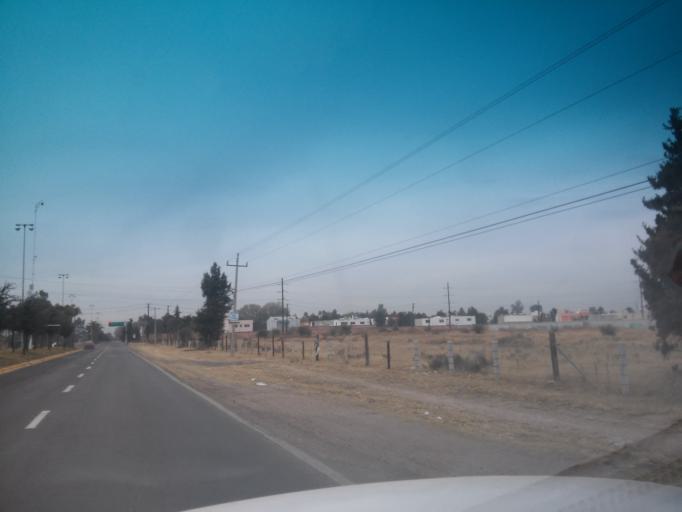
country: MX
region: Durango
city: Victoria de Durango
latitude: 23.9973
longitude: -104.6407
